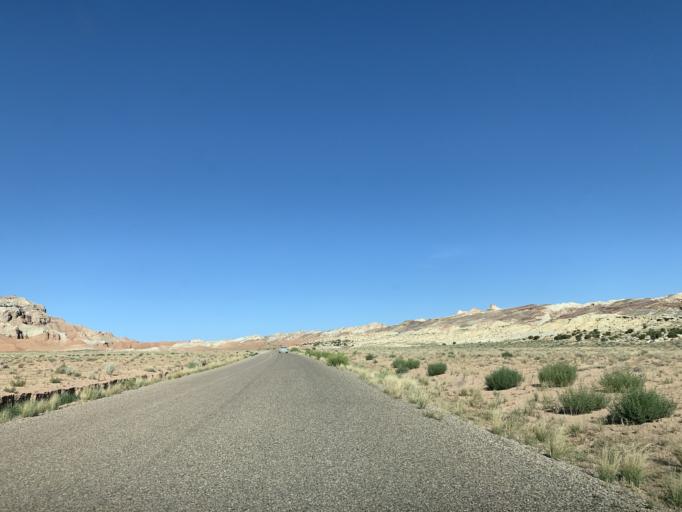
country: US
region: Utah
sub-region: Emery County
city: Ferron
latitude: 38.5787
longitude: -110.7655
